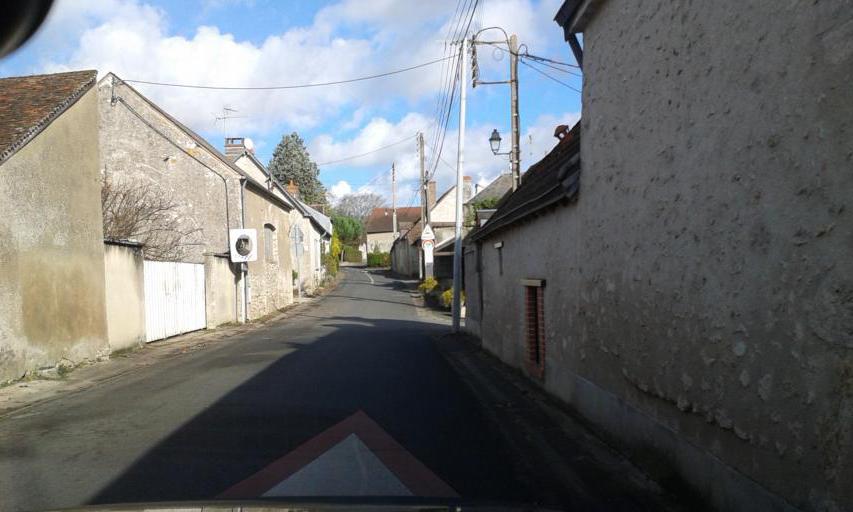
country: FR
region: Centre
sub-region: Departement du Loir-et-Cher
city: Saint-Laurent-Nouan
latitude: 47.7318
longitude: 1.5850
